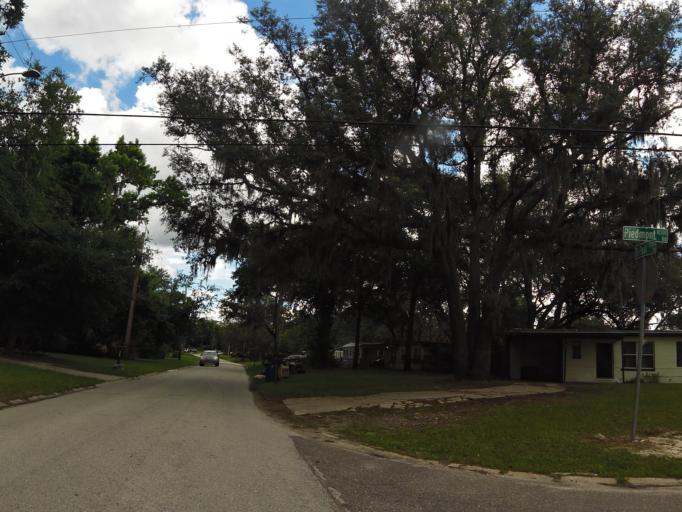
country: US
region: Florida
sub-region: Duval County
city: Jacksonville
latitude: 30.4212
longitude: -81.6701
